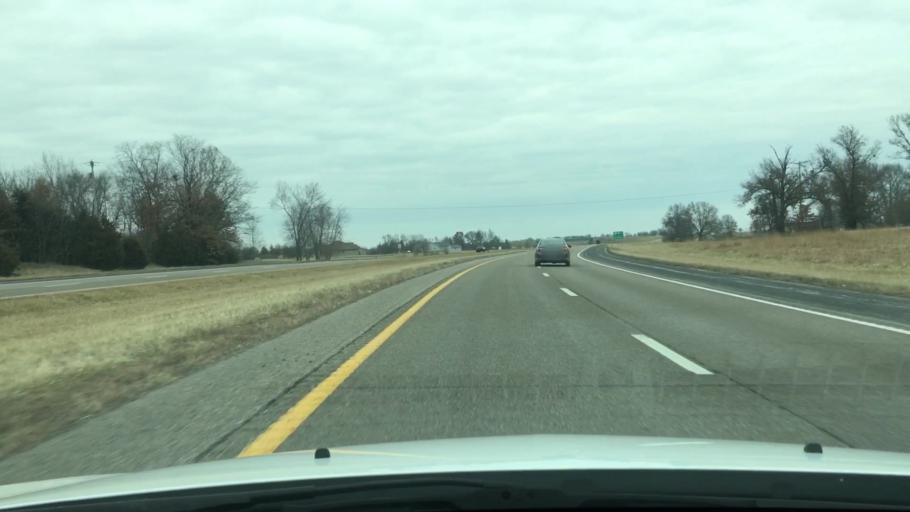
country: US
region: Missouri
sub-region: Audrain County
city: Mexico
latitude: 39.0098
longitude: -91.8921
